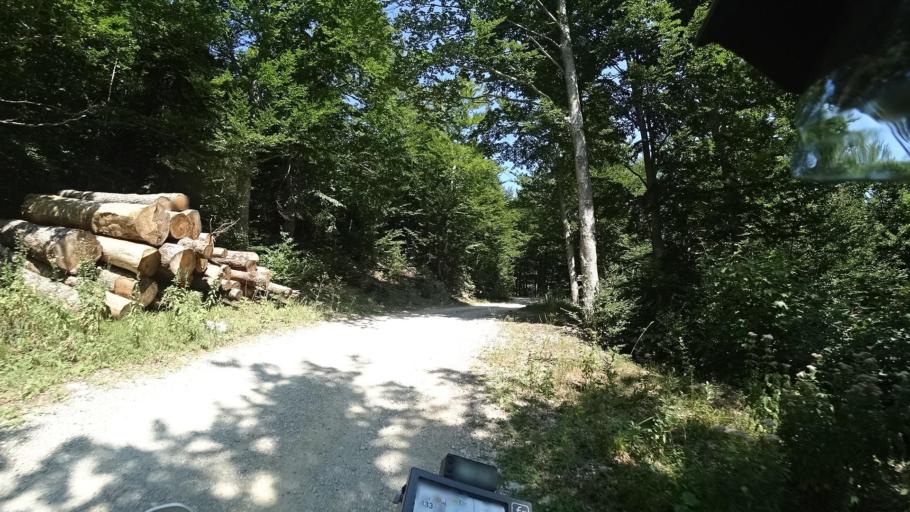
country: HR
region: Licko-Senjska
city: Popovaca
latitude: 44.5908
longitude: 15.1777
